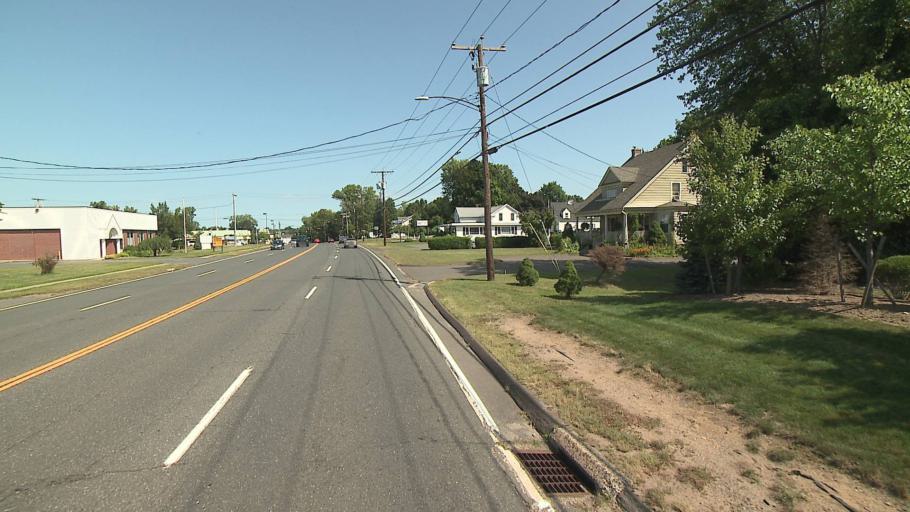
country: US
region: Connecticut
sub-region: Hartford County
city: Thompsonville
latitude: 42.0049
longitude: -72.5925
